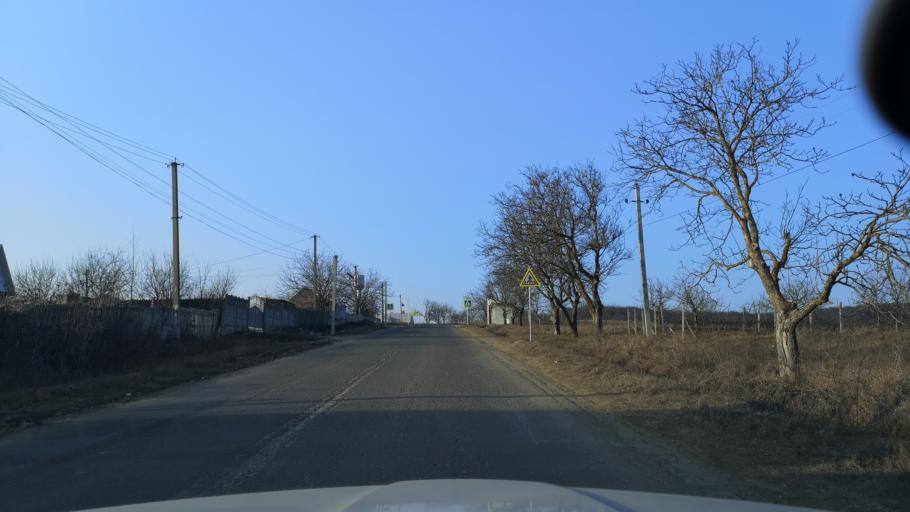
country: MD
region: Stinga Nistrului
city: Bucovat
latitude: 47.1236
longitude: 28.5032
